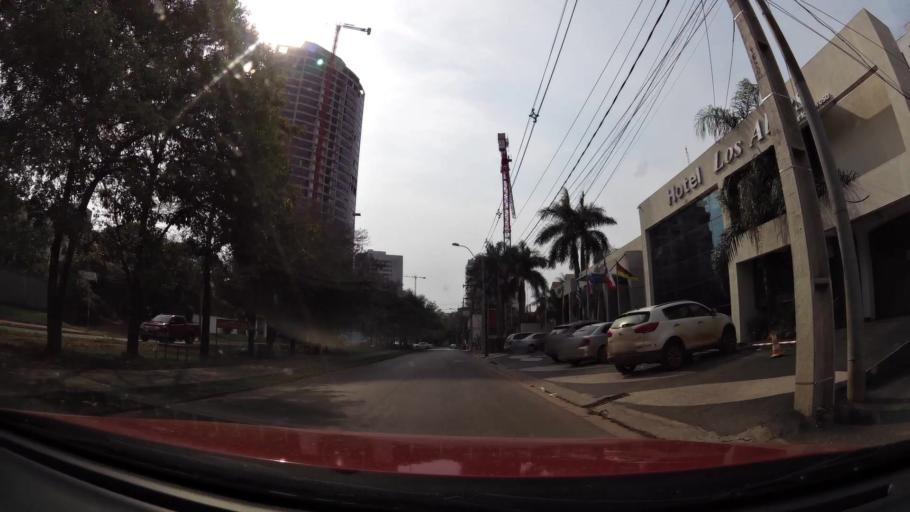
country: PY
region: Central
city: Fernando de la Mora
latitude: -25.2878
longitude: -57.5558
